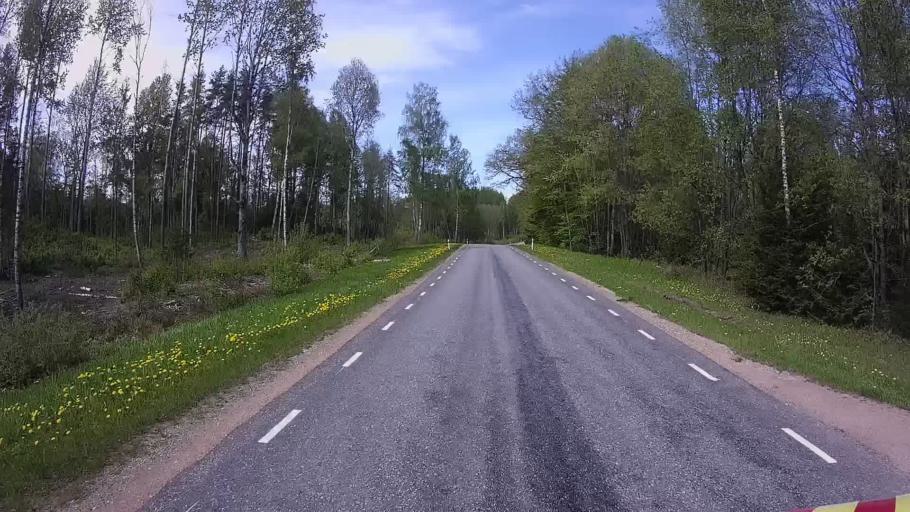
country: EE
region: Valgamaa
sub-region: Valga linn
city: Valga
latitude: 57.6774
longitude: 26.2826
